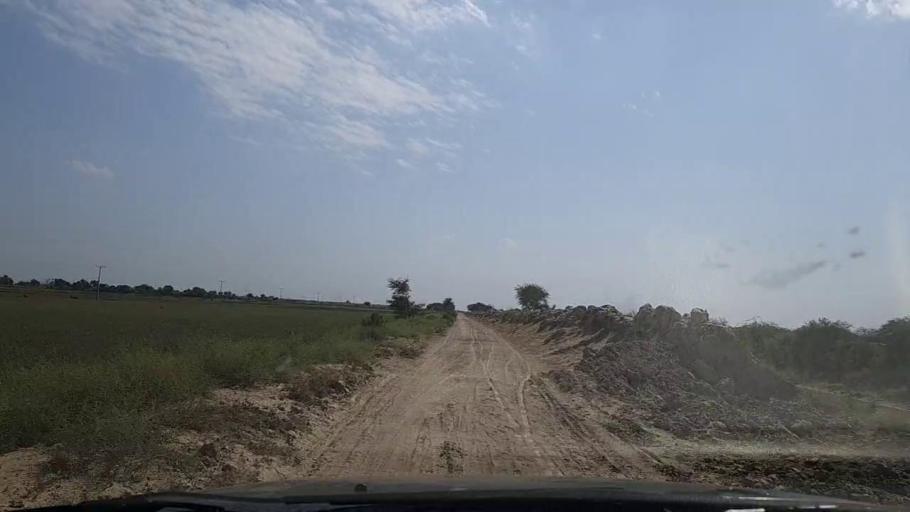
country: PK
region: Sindh
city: Mirpur Batoro
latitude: 24.5858
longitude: 68.1967
